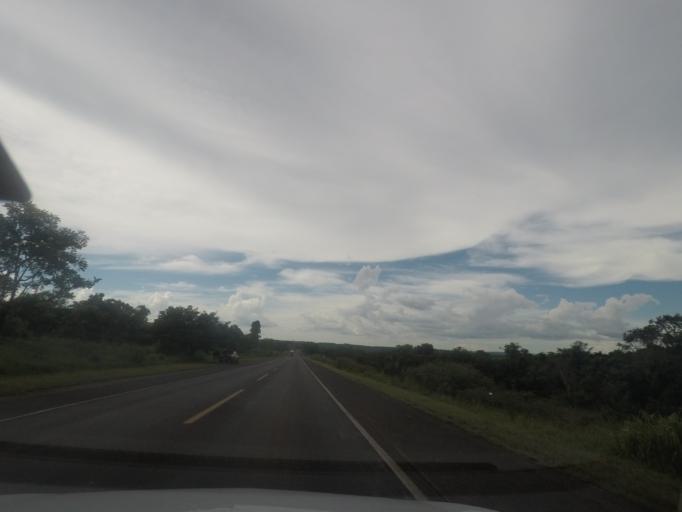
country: BR
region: Minas Gerais
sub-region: Prata
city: Prata
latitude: -19.3704
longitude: -48.8992
